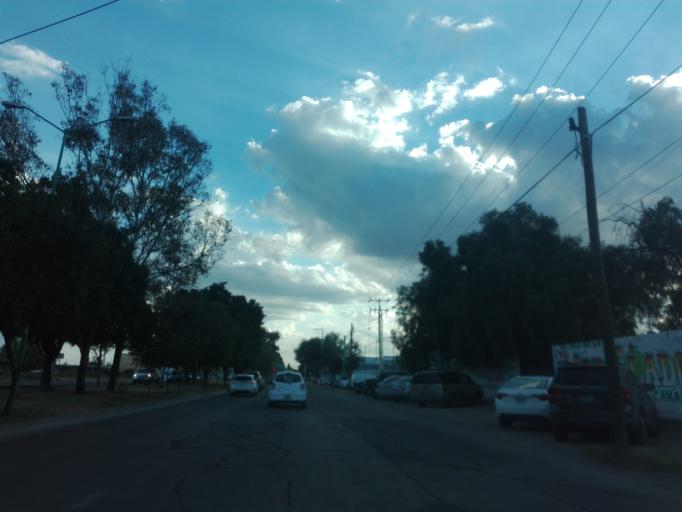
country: MX
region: Guanajuato
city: Leon
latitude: 21.1011
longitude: -101.6615
